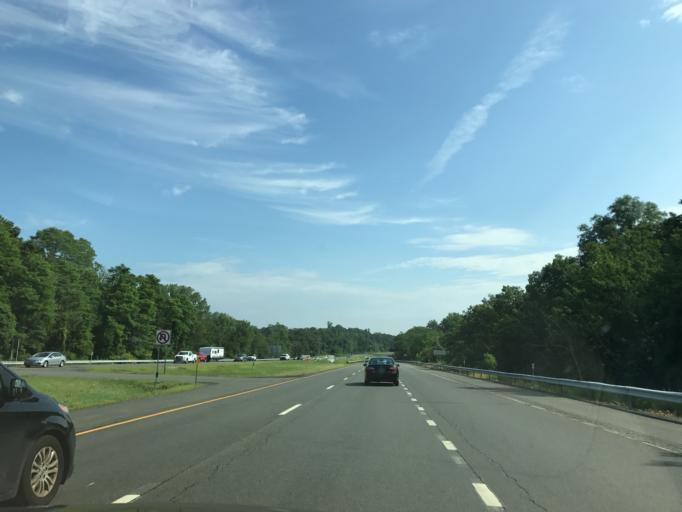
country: US
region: New York
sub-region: Rockland County
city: Chestnut Ridge
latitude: 41.0731
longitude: -74.0519
